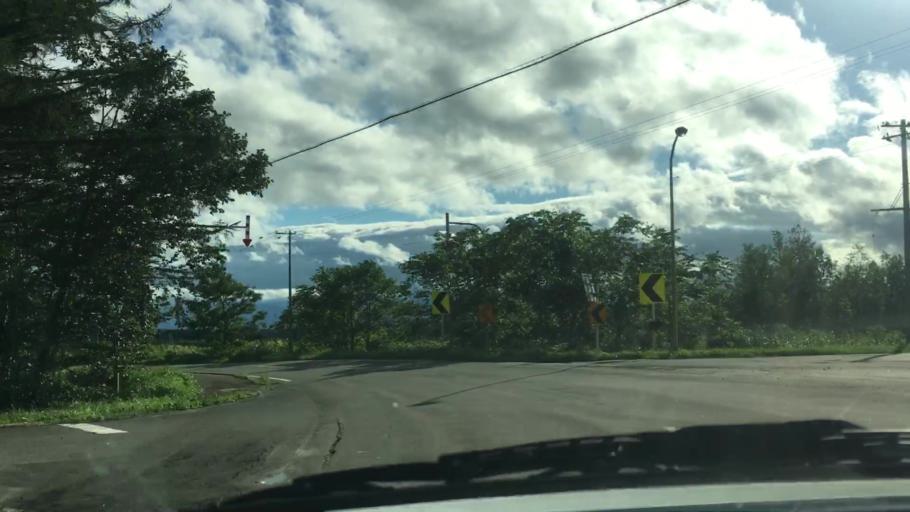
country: JP
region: Hokkaido
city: Otofuke
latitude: 43.1792
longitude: 143.0083
